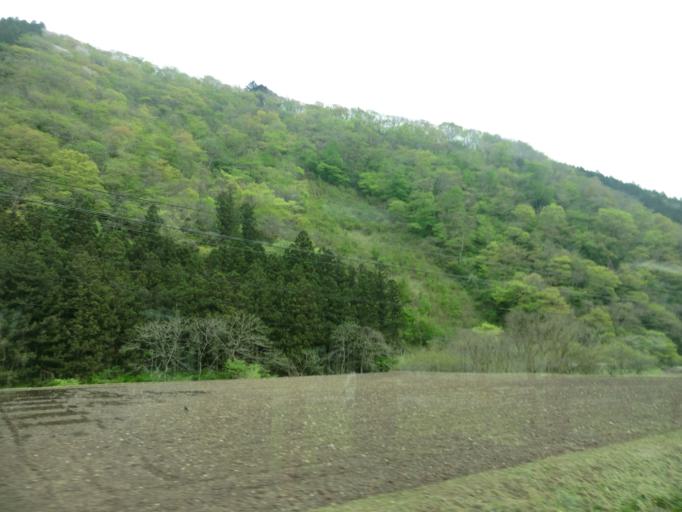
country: JP
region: Miyagi
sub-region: Oshika Gun
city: Onagawa Cho
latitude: 38.6424
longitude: 141.3879
